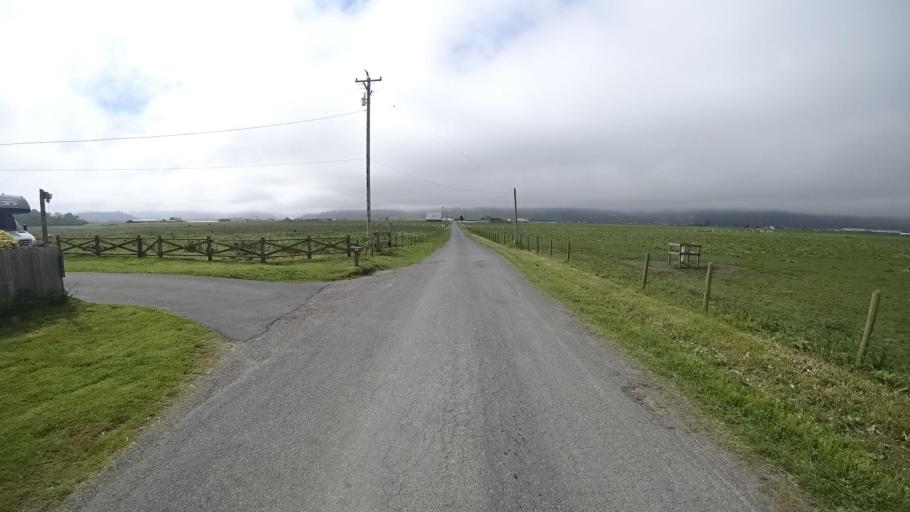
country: US
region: California
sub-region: Humboldt County
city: Fortuna
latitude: 40.5831
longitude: -124.1879
